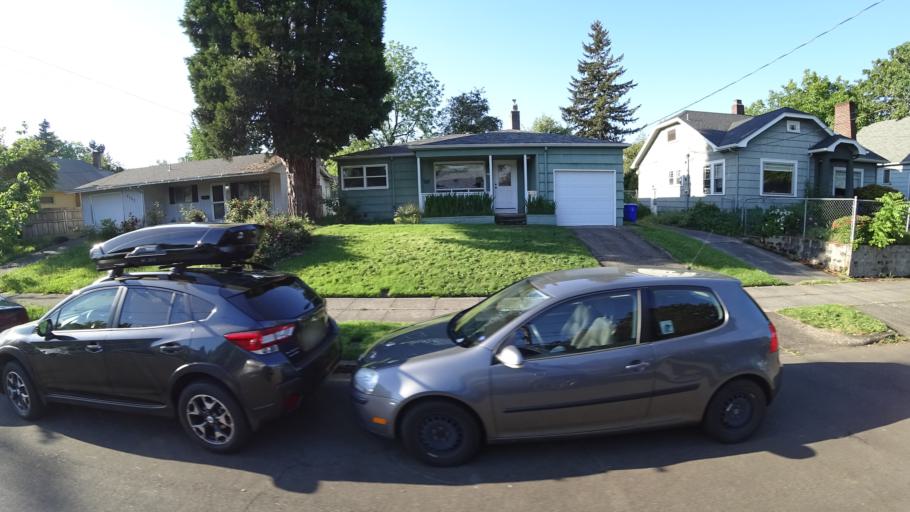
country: US
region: Oregon
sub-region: Multnomah County
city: Portland
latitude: 45.5577
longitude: -122.6890
